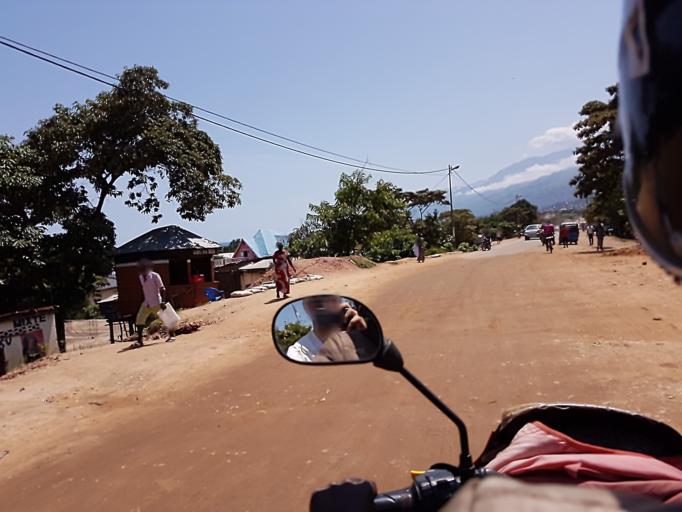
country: CD
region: South Kivu
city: Uvira
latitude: -3.3555
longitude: 29.1541
